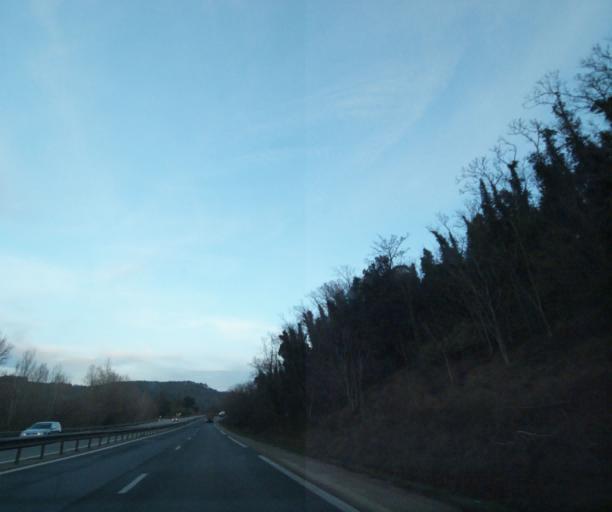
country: FR
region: Provence-Alpes-Cote d'Azur
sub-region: Departement du Var
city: Trans-en-Provence
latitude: 43.4934
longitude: 6.4990
